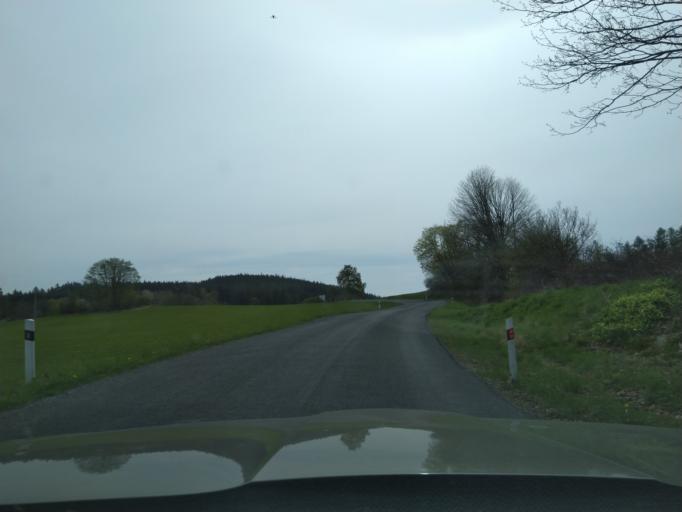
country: CZ
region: Jihocesky
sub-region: Okres Prachatice
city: Stachy
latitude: 49.1809
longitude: 13.6514
